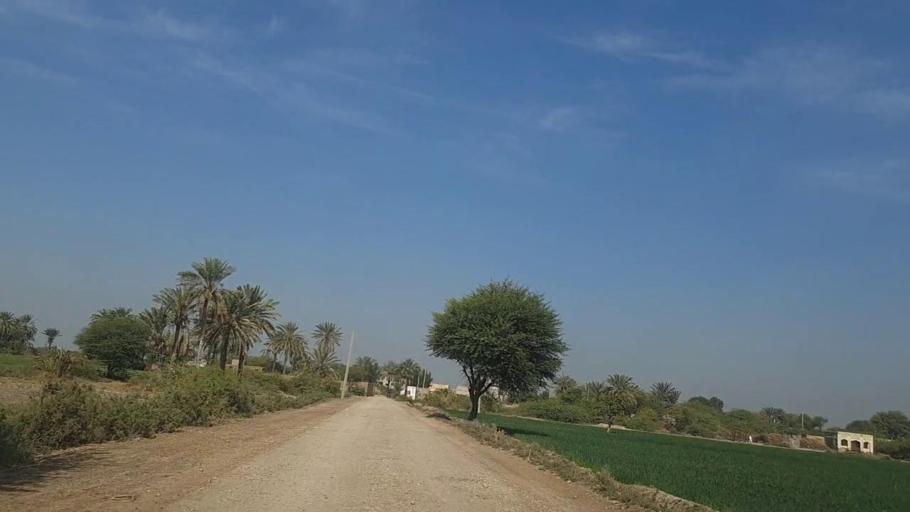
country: PK
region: Sindh
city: Mirpur Khas
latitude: 25.4878
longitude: 68.9653
